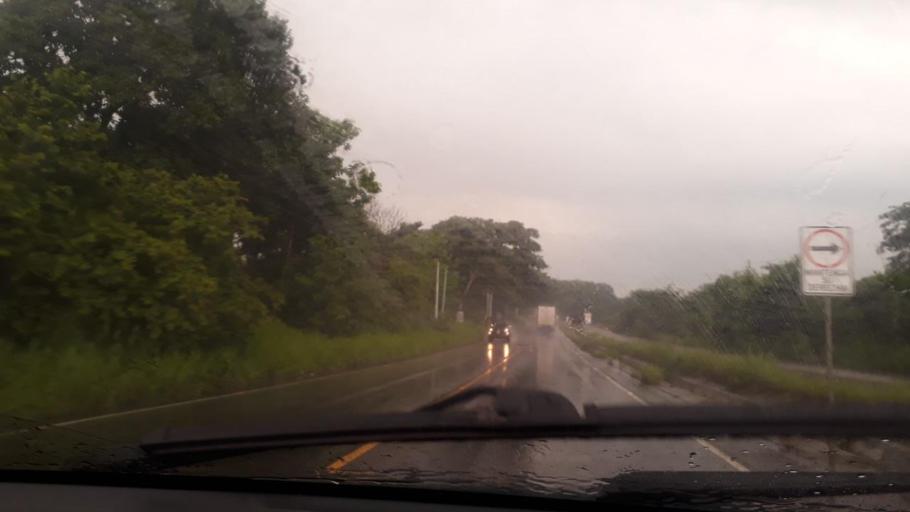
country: GT
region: Santa Rosa
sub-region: Municipio de Taxisco
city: Taxisco
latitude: 14.0959
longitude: -90.5287
